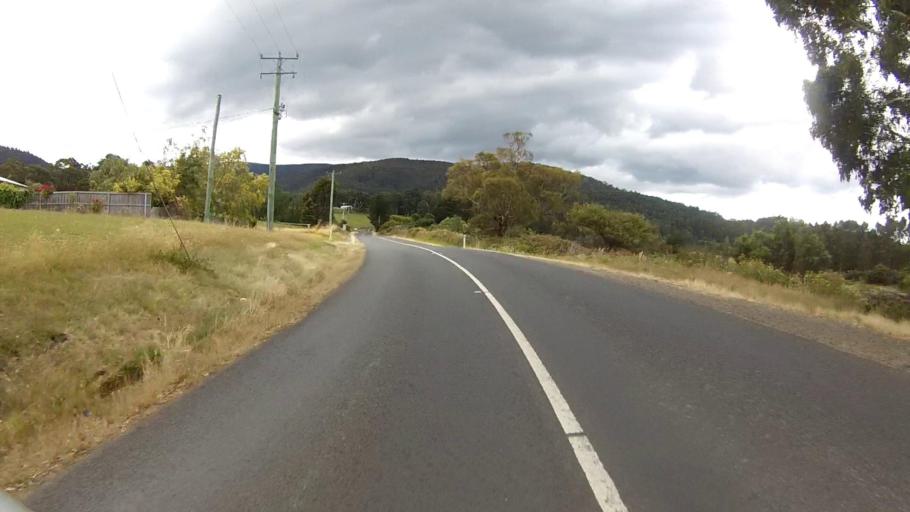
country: AU
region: Tasmania
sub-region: Kingborough
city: Margate
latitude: -42.9619
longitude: 147.2130
